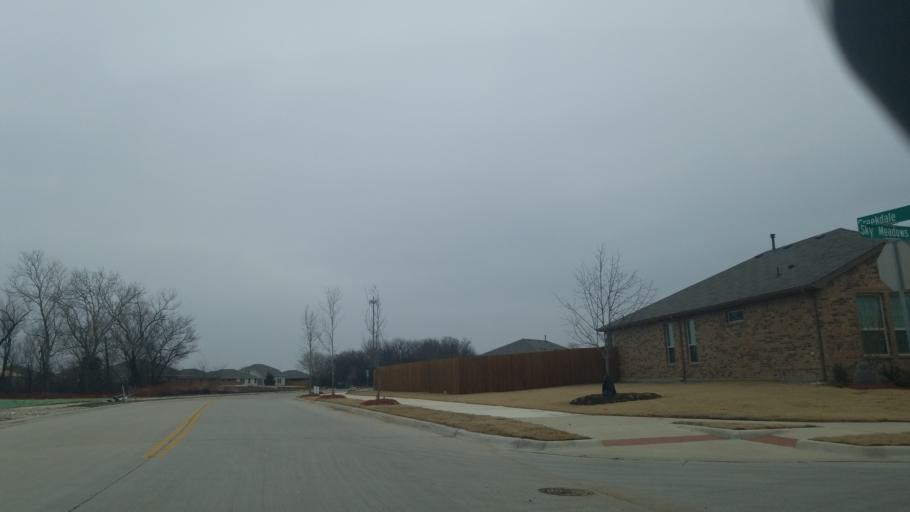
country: US
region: Texas
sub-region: Denton County
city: Denton
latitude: 33.1581
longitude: -97.1363
